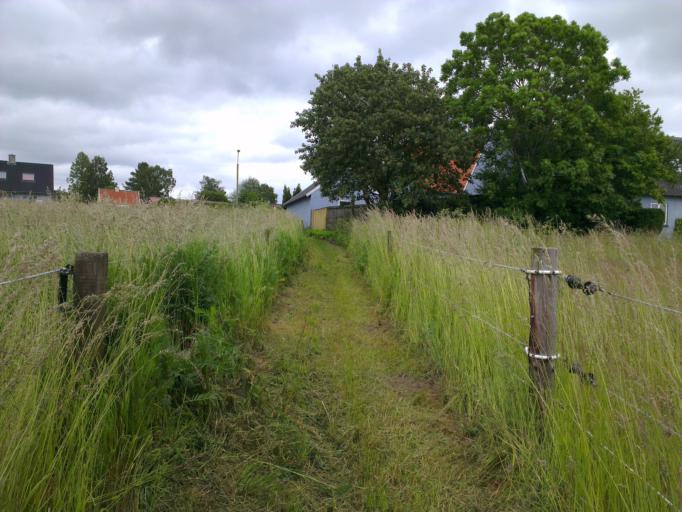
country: DK
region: Capital Region
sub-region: Frederikssund Kommune
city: Jaegerspris
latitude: 55.8359
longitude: 11.9875
